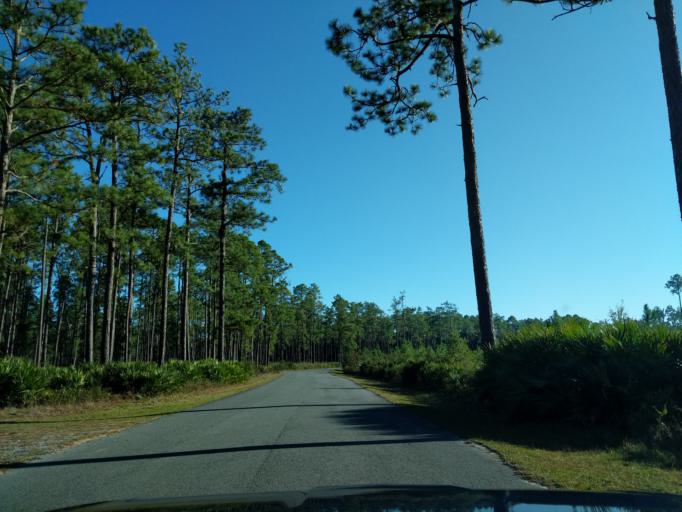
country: US
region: Georgia
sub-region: Charlton County
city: Folkston
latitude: 30.7375
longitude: -82.1367
